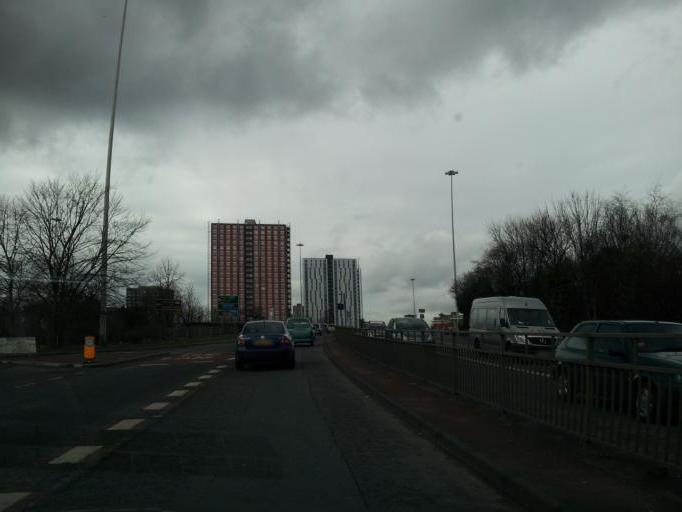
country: GB
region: England
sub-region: City and Borough of Salford
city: Salford
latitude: 53.4847
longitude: -2.2738
